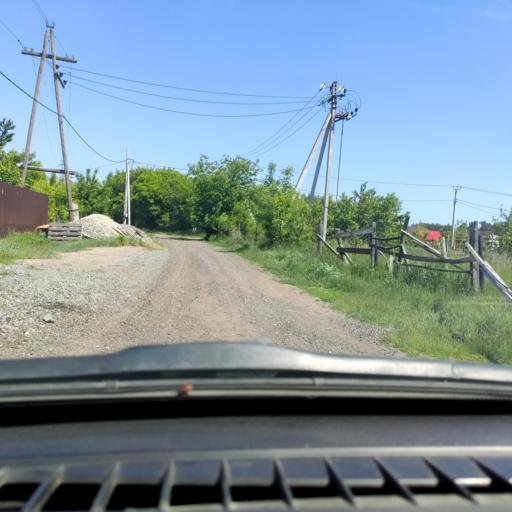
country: RU
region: Samara
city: Povolzhskiy
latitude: 53.5857
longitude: 49.5670
